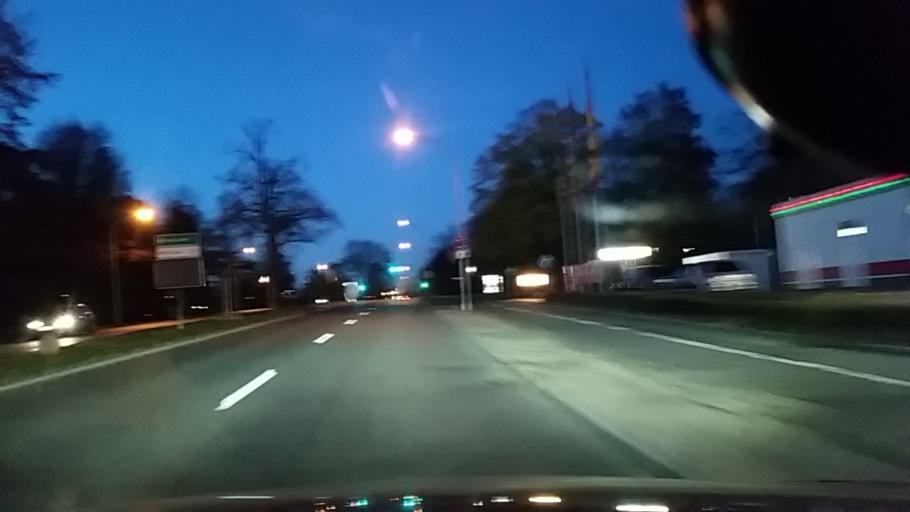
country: DE
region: Lower Saxony
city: Wolfsburg
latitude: 52.4404
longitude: 10.8077
